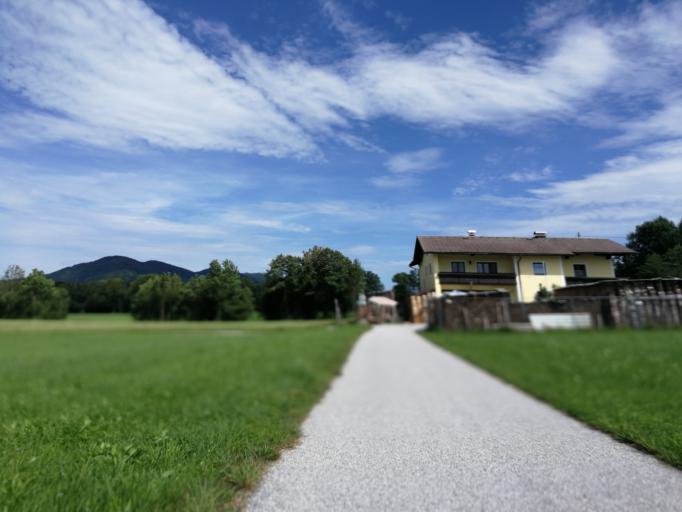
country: AT
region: Salzburg
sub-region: Politischer Bezirk Salzburg-Umgebung
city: Plainfeld
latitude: 47.8603
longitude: 13.1610
